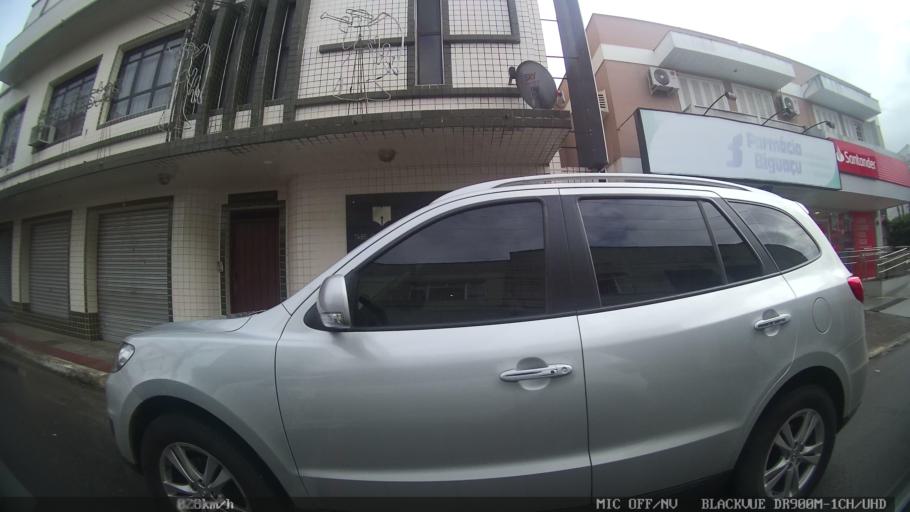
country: BR
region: Santa Catarina
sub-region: Biguacu
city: Biguacu
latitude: -27.4951
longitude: -48.6545
